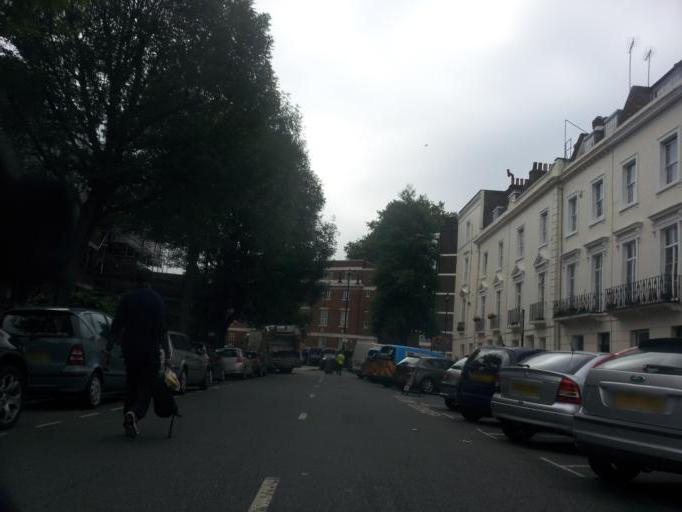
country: GB
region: England
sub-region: Greater London
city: London
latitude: 51.4896
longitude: -0.1351
